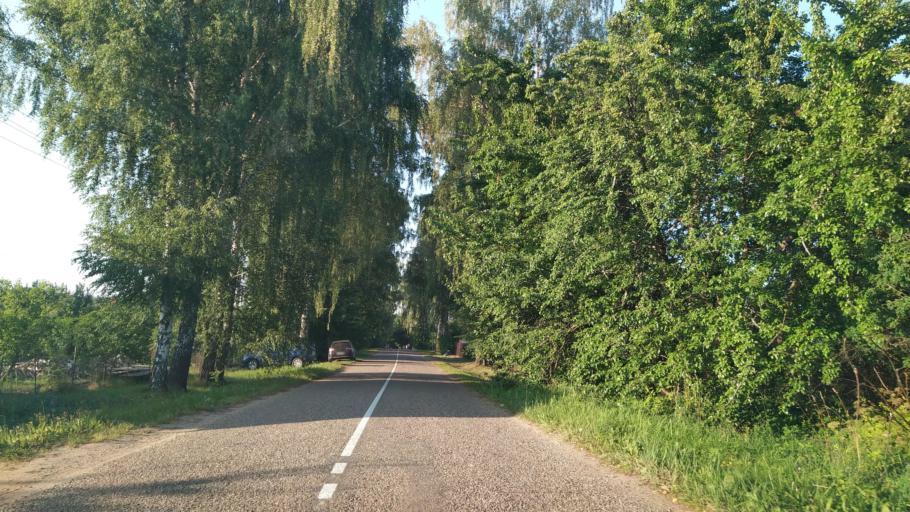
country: RU
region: Pskov
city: Pushkinskiye Gory
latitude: 57.0433
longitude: 28.9161
